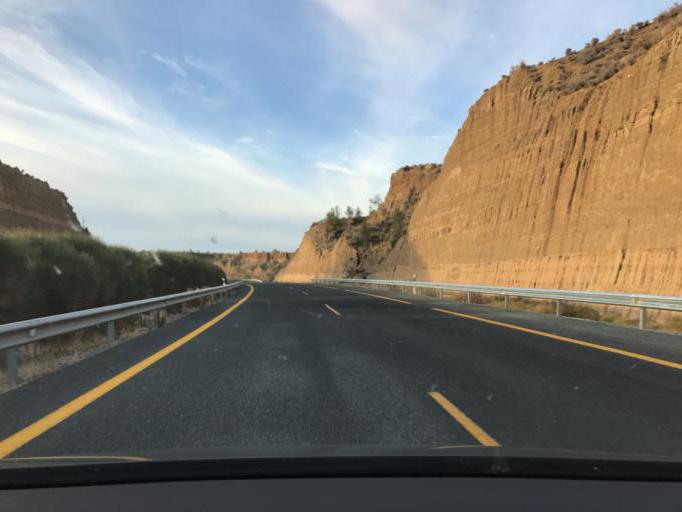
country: ES
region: Andalusia
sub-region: Provincia de Granada
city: Guadix
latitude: 37.3172
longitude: -3.1127
